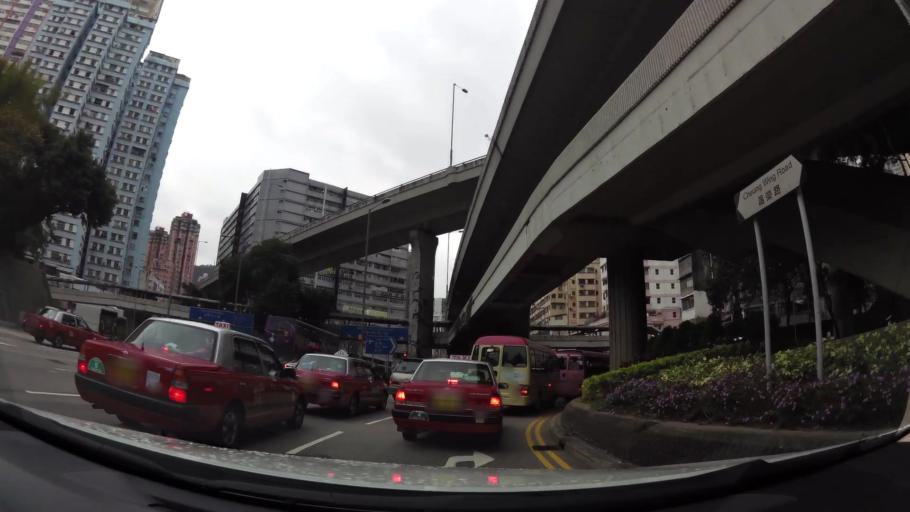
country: HK
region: Tsuen Wan
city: Tsuen Wan
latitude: 22.3691
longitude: 114.1343
